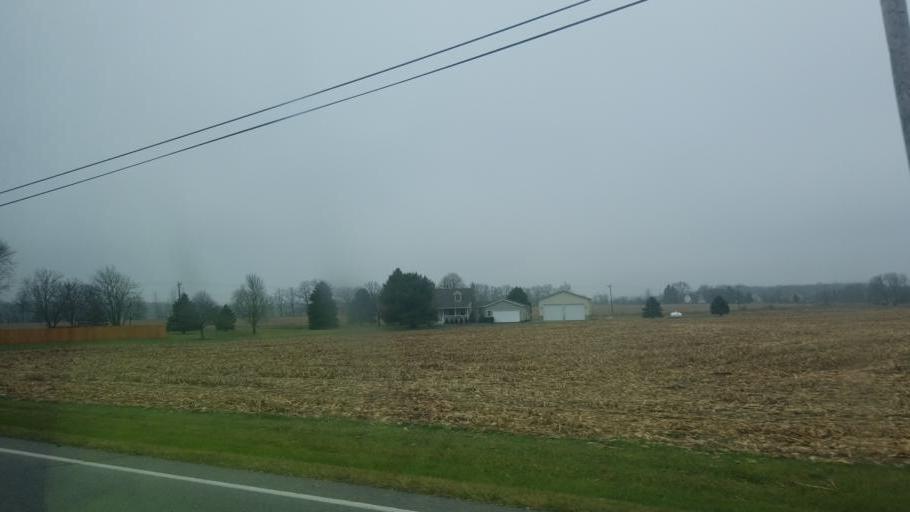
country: US
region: Ohio
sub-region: Union County
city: New California
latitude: 40.1824
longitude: -83.2764
